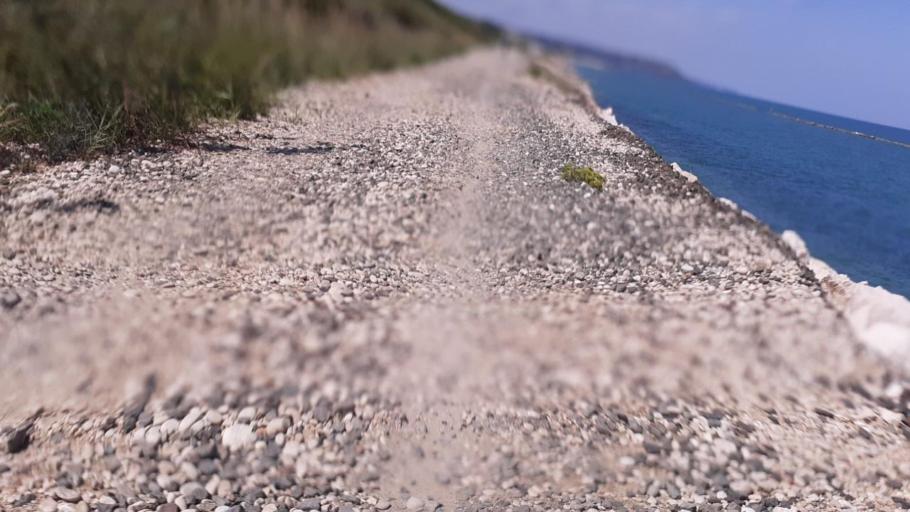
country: IT
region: Abruzzo
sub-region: Provincia di Chieti
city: Torino di Sangro
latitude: 42.2227
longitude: 14.5650
